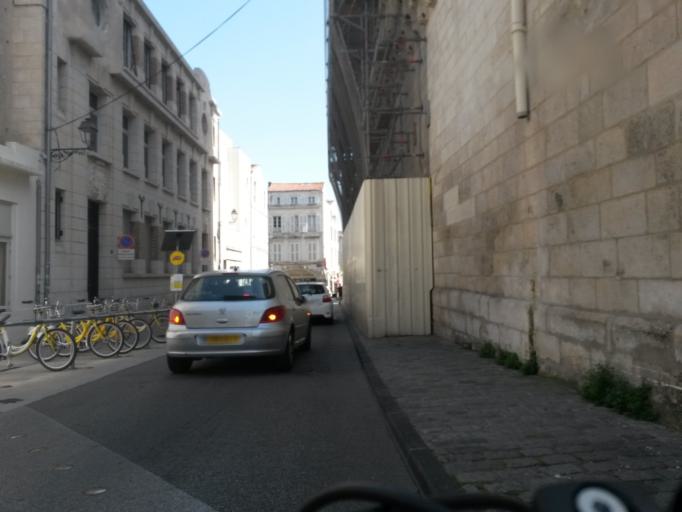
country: FR
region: Poitou-Charentes
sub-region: Departement de la Charente-Maritime
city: La Rochelle
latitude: 46.1598
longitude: -1.1515
